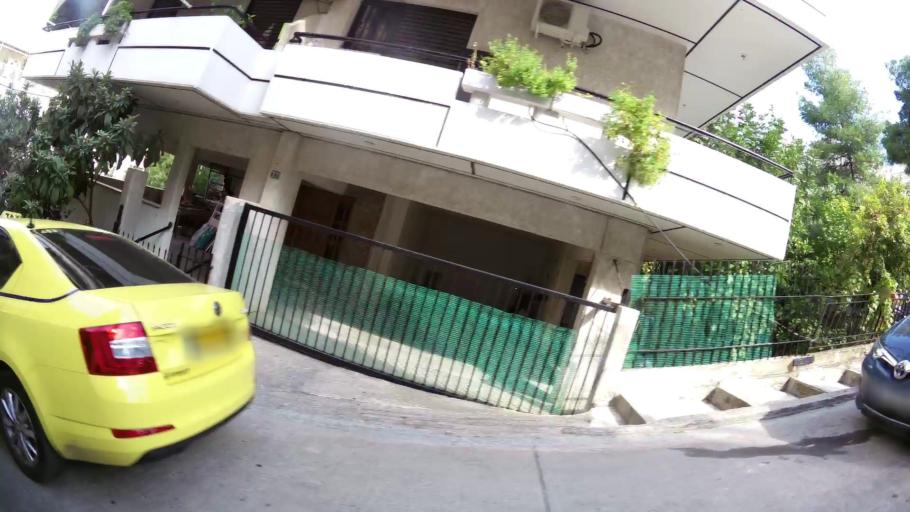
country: GR
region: Attica
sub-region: Nomarchia Athinas
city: Galatsi
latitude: 38.0112
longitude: 23.7593
